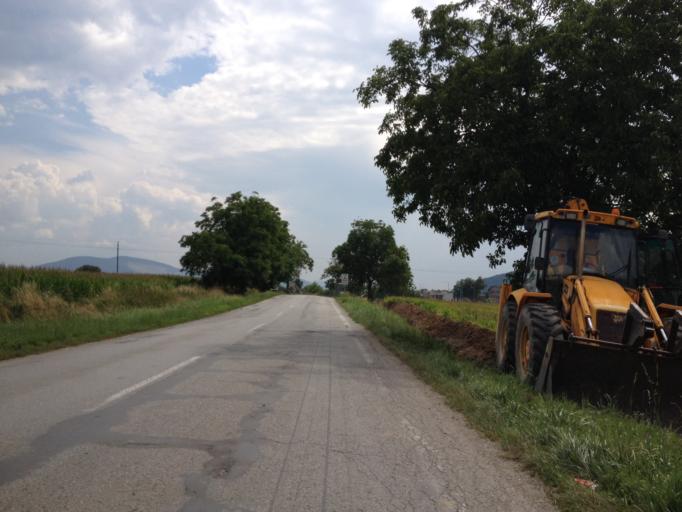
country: SK
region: Nitriansky
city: Puchov
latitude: 49.1031
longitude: 18.3259
